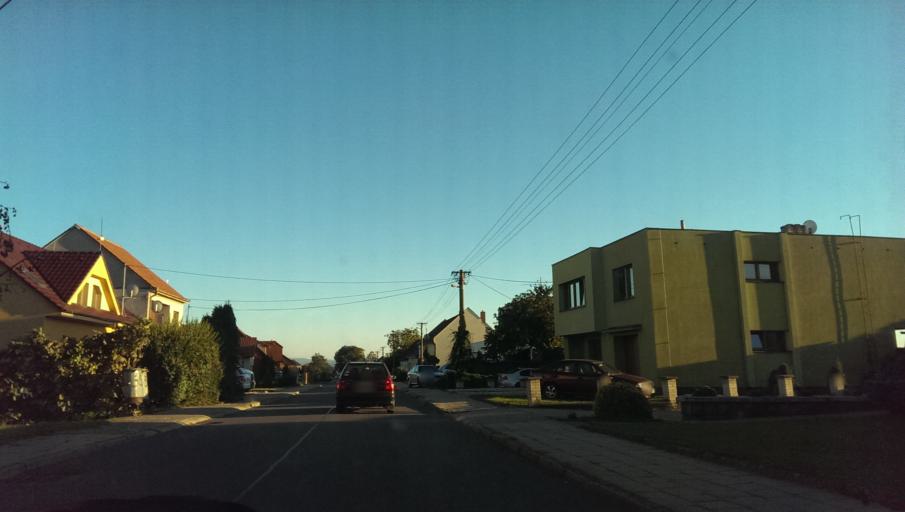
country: CZ
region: Zlin
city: Tupesy
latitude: 49.0817
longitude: 17.3757
